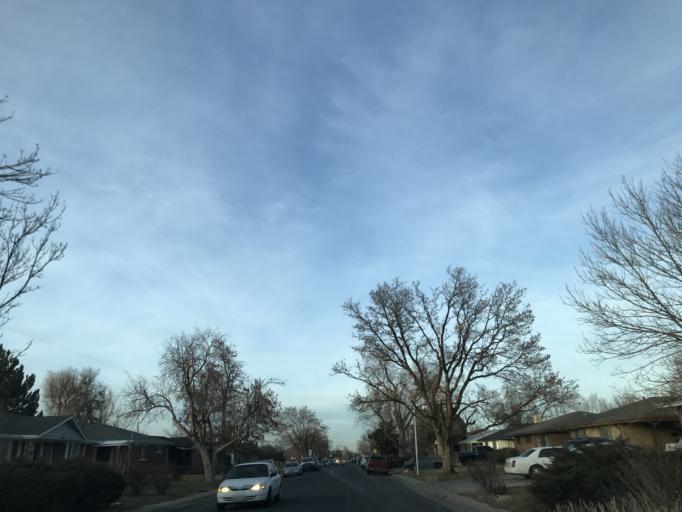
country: US
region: Colorado
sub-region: Adams County
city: Aurora
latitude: 39.7514
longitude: -104.8646
